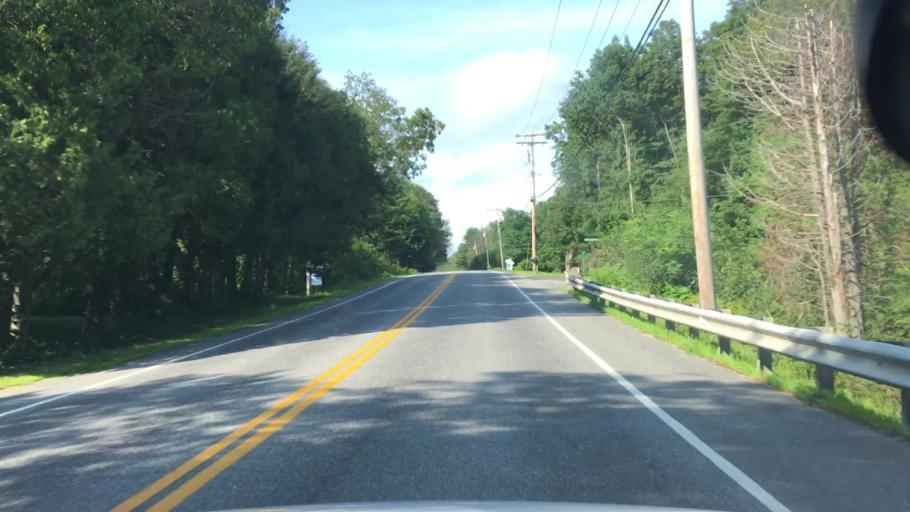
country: US
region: Maine
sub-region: Cumberland County
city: Harpswell Center
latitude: 43.8254
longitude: -69.9189
